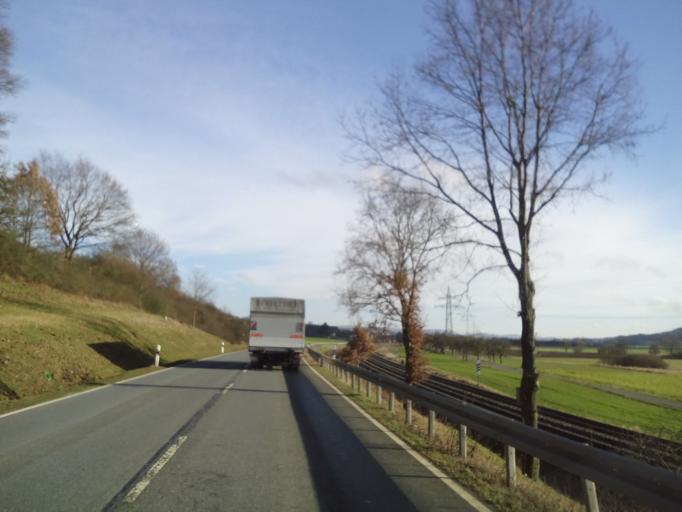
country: DE
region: Bavaria
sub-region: Upper Franconia
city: Altenkunstadt
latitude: 50.1249
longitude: 11.3050
